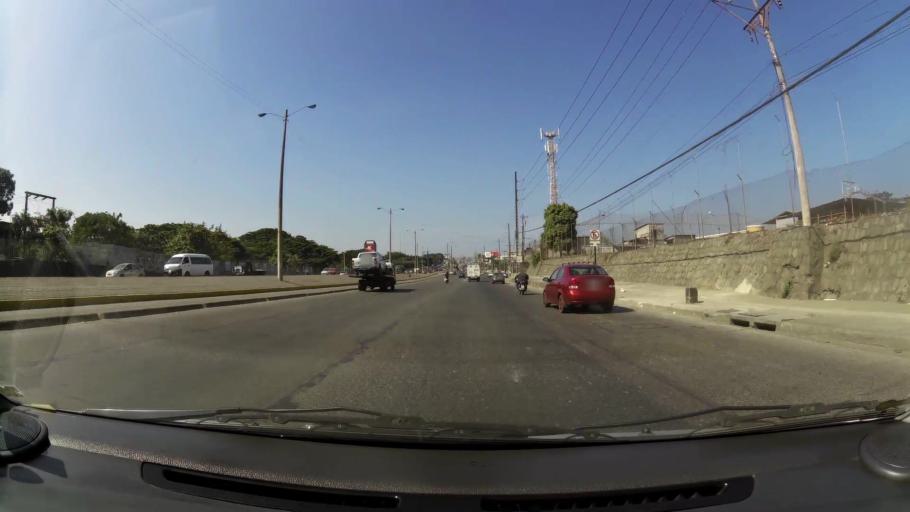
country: EC
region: Guayas
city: Guayaquil
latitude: -2.1135
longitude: -79.9333
